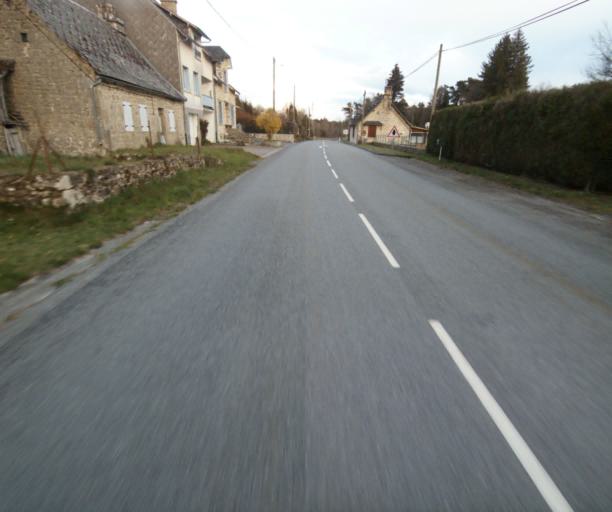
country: FR
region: Limousin
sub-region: Departement de la Correze
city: Correze
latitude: 45.2791
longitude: 1.9499
